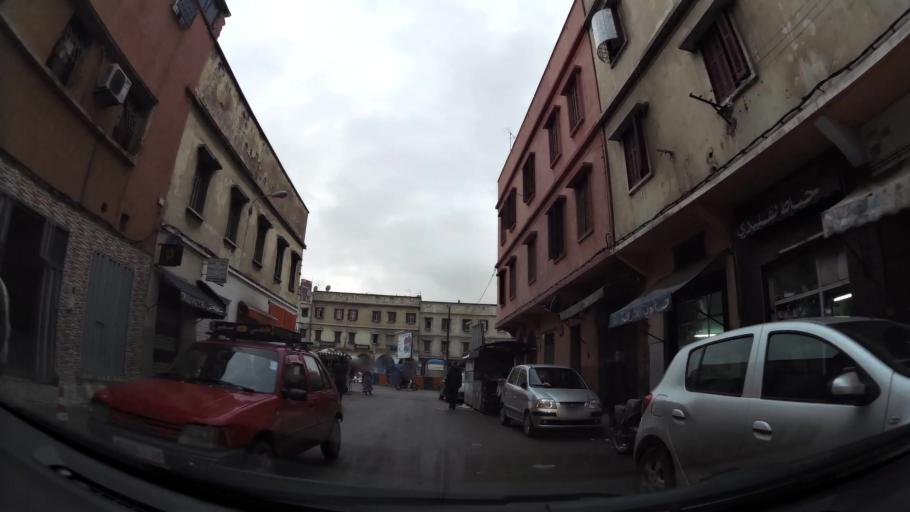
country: MA
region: Grand Casablanca
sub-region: Casablanca
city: Casablanca
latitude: 33.5693
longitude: -7.6005
